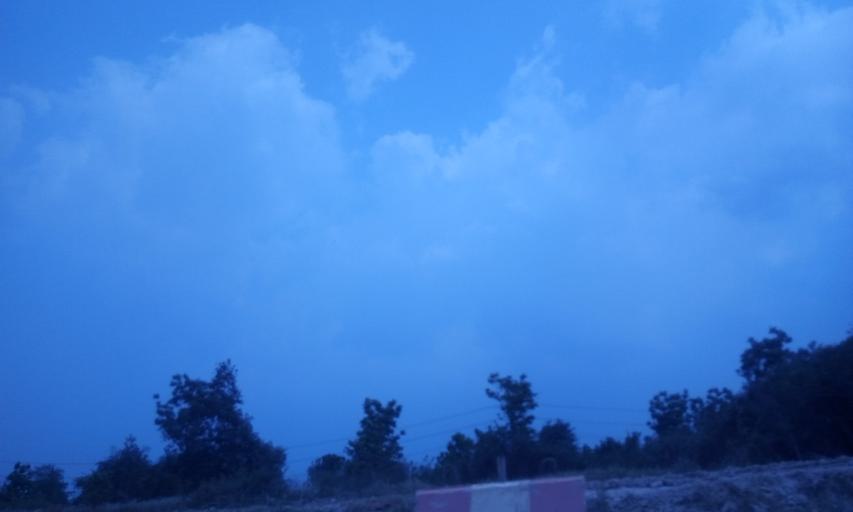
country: TH
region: Chon Buri
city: Ban Bueng
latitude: 13.3298
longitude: 101.1879
